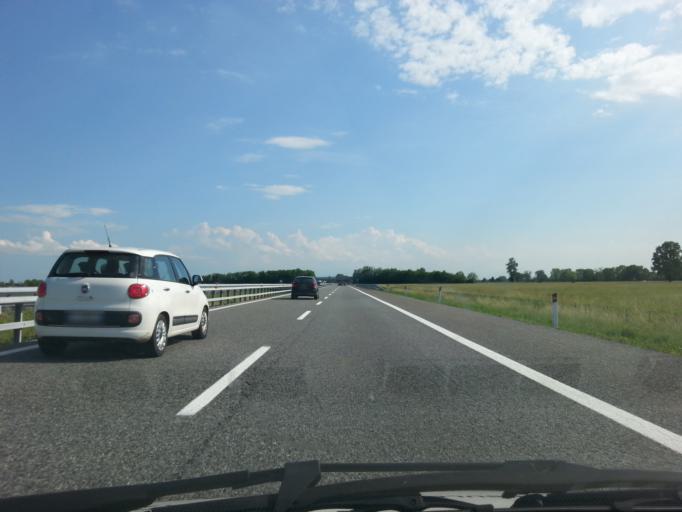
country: IT
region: Piedmont
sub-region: Provincia di Cuneo
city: Caramagna Piemonte
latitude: 44.7632
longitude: 7.7507
